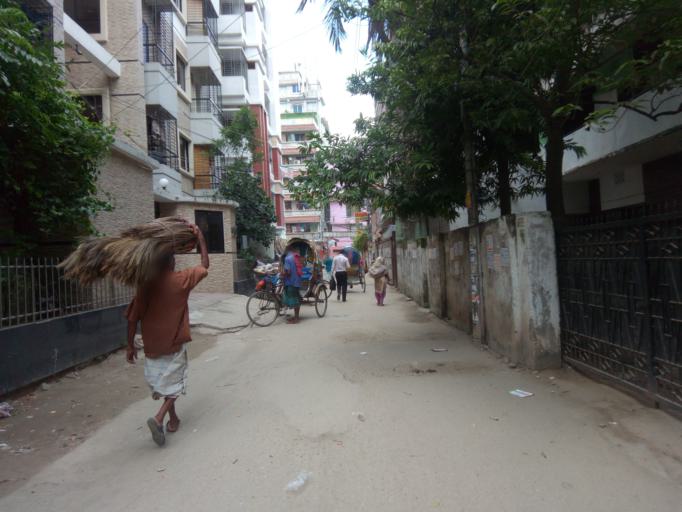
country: BD
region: Dhaka
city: Azimpur
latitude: 23.7442
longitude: 90.3885
